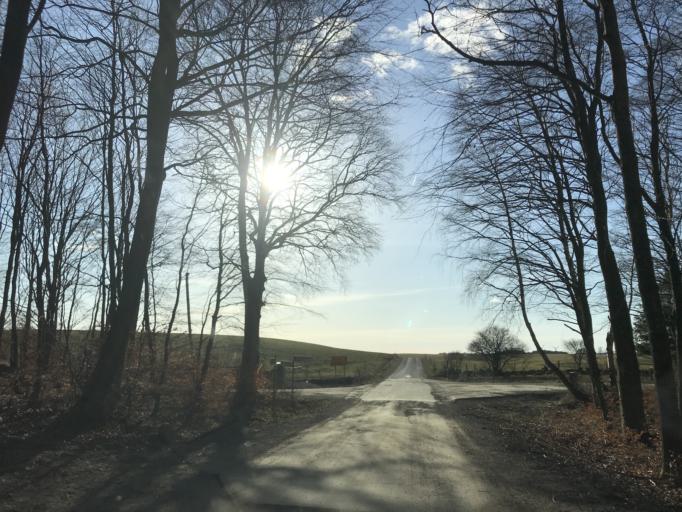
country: SE
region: Skane
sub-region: Ystads Kommun
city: Ystad
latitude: 55.5572
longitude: 13.8160
